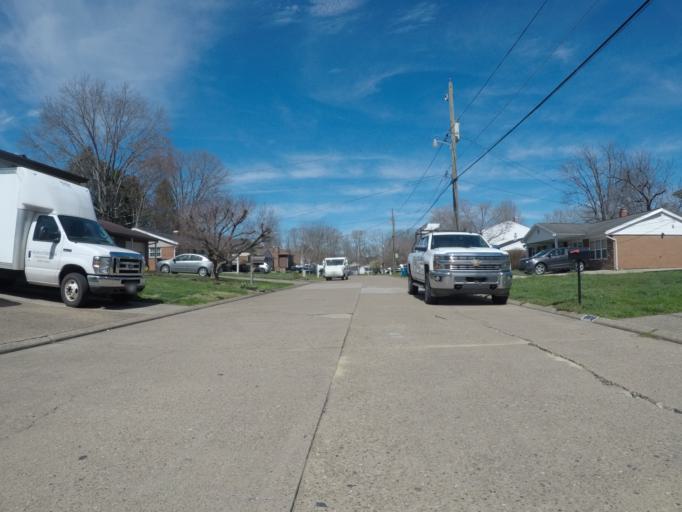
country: US
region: West Virginia
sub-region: Cabell County
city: Pea Ridge
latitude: 38.4021
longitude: -82.3148
